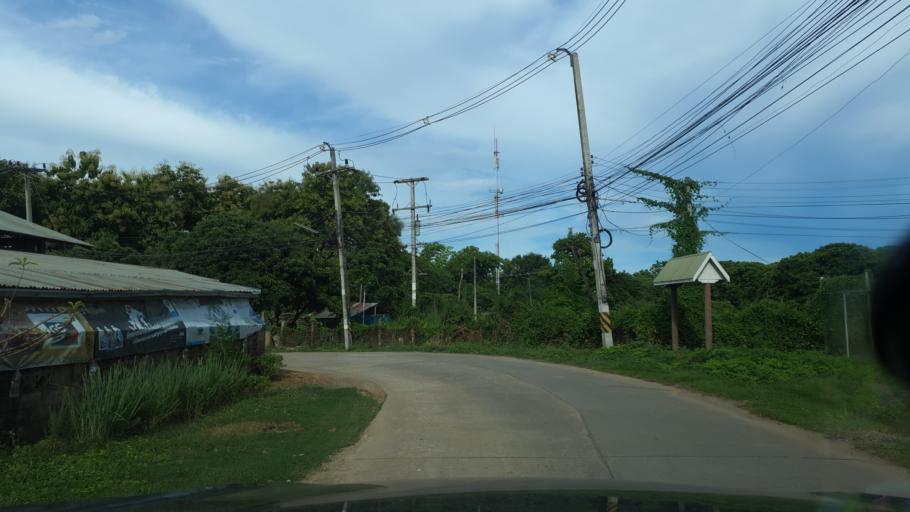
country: TH
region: Sukhothai
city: Thung Saliam
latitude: 17.3199
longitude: 99.5648
